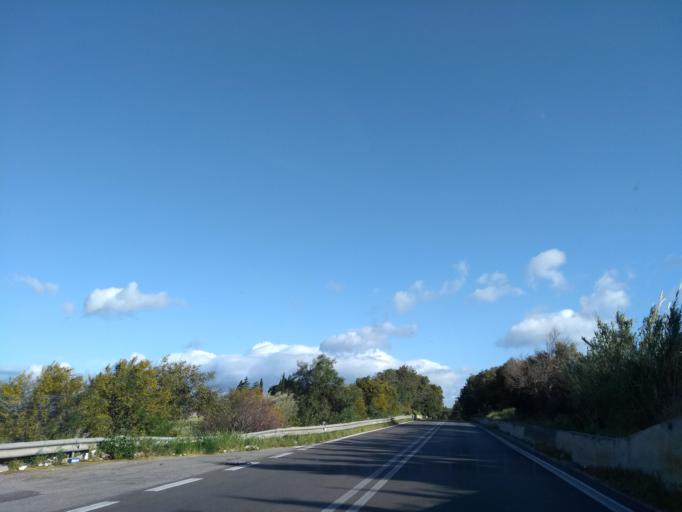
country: IT
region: Sicily
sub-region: Trapani
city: Alcamo
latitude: 38.0107
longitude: 12.9611
